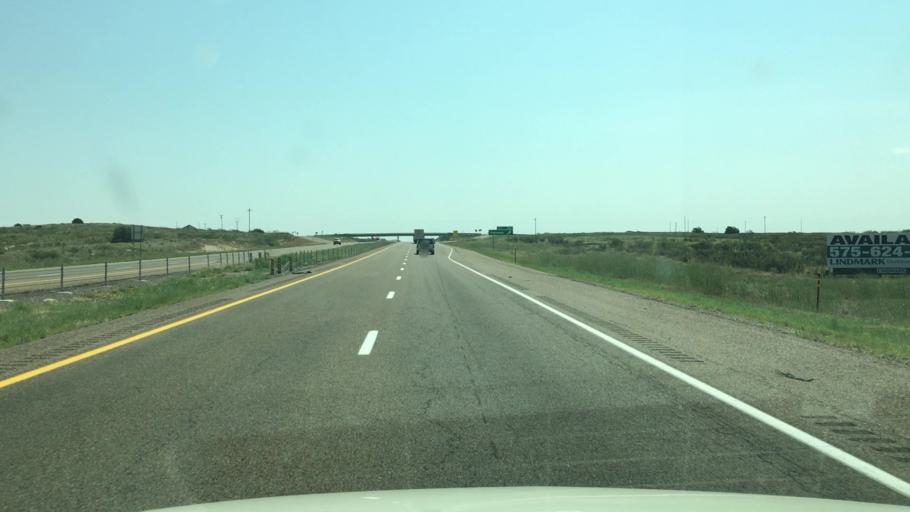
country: US
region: New Mexico
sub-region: Quay County
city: Tucumcari
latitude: 35.1198
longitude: -103.9003
